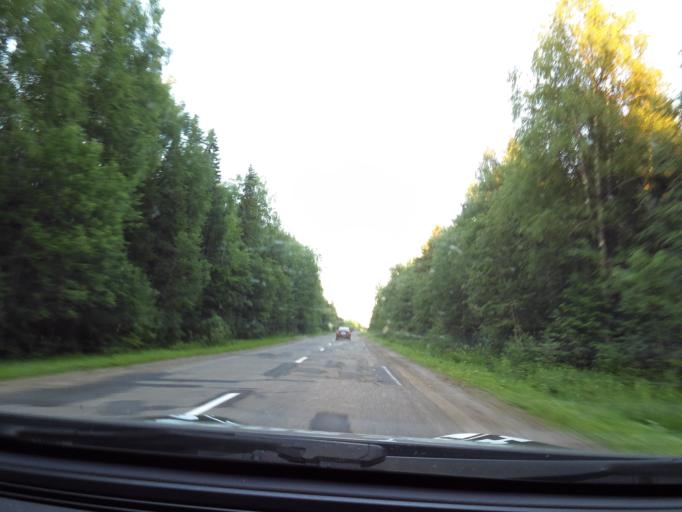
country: RU
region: Jaroslavl
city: Prechistoye
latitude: 58.3944
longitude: 40.4203
